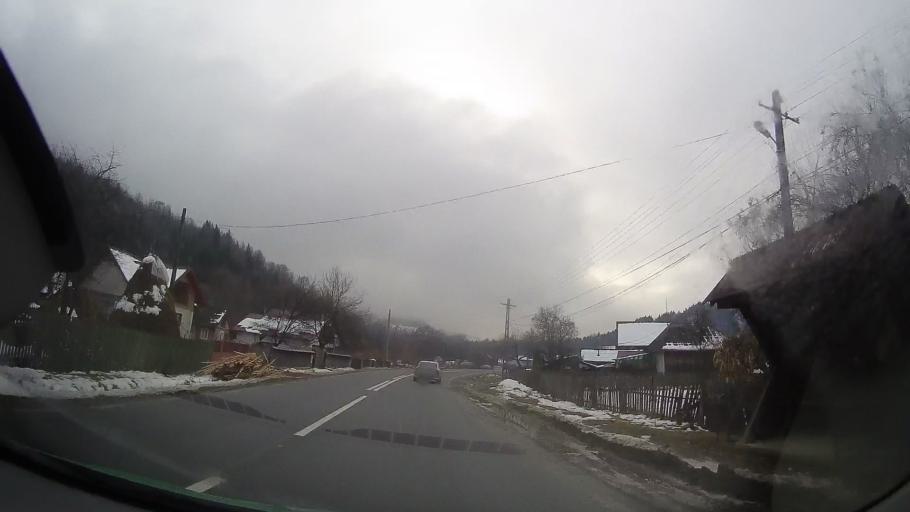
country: RO
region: Neamt
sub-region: Comuna Bicazu Ardelean
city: Bicazu Ardelean
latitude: 46.8651
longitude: 25.9408
